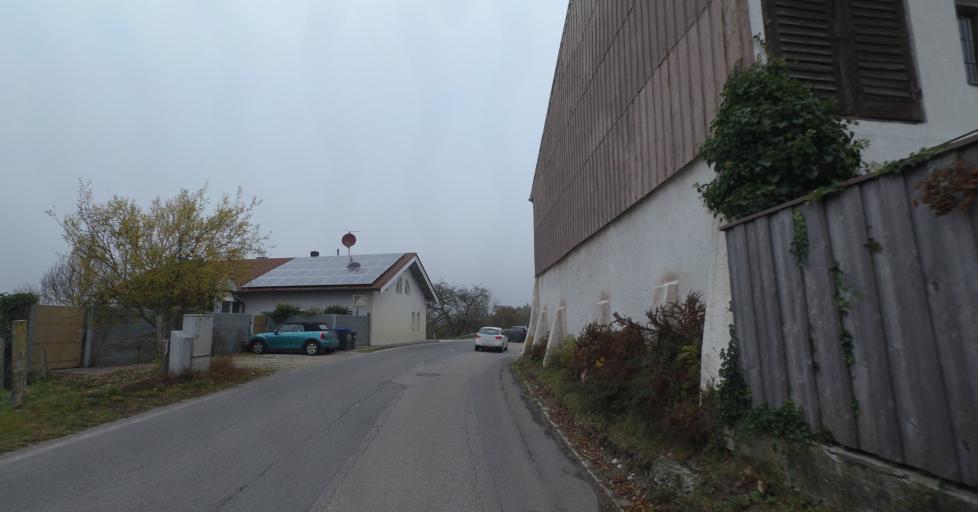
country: DE
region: Bavaria
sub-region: Upper Bavaria
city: Trostberg an der Alz
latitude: 47.9790
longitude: 12.5261
